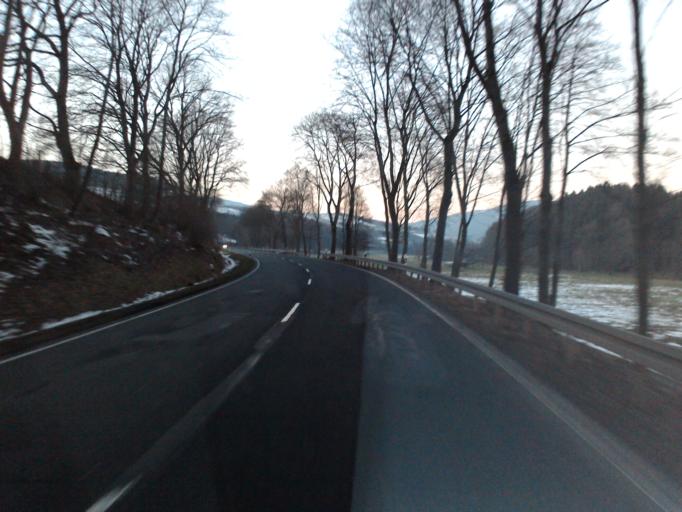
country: DE
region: North Rhine-Westphalia
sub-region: Regierungsbezirk Arnsberg
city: Olsberg
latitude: 51.2939
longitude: 8.4996
